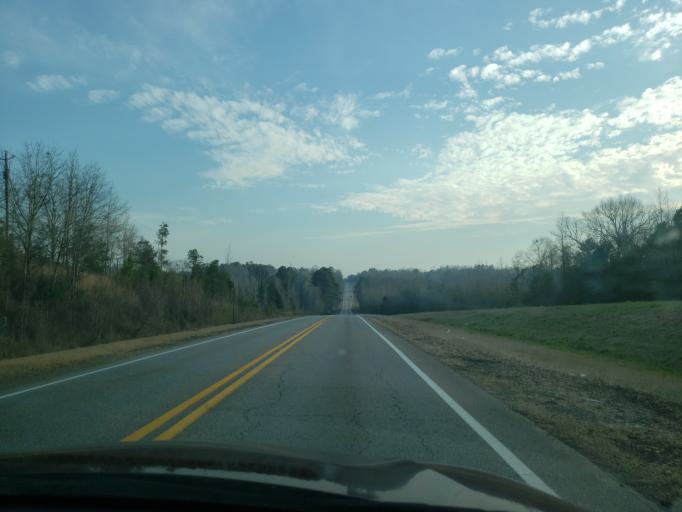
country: US
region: Alabama
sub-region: Hale County
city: Moundville
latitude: 32.9275
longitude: -87.6361
